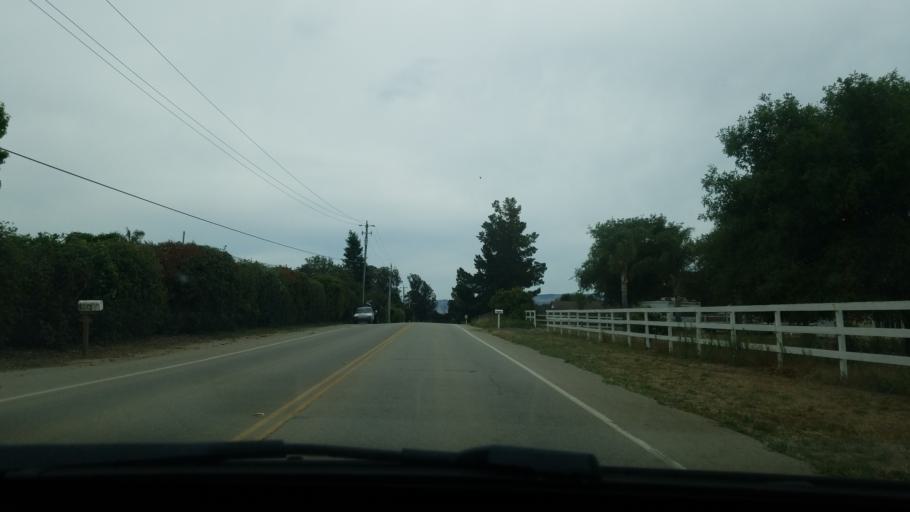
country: US
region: California
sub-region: San Luis Obispo County
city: Nipomo
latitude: 35.0136
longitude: -120.4931
